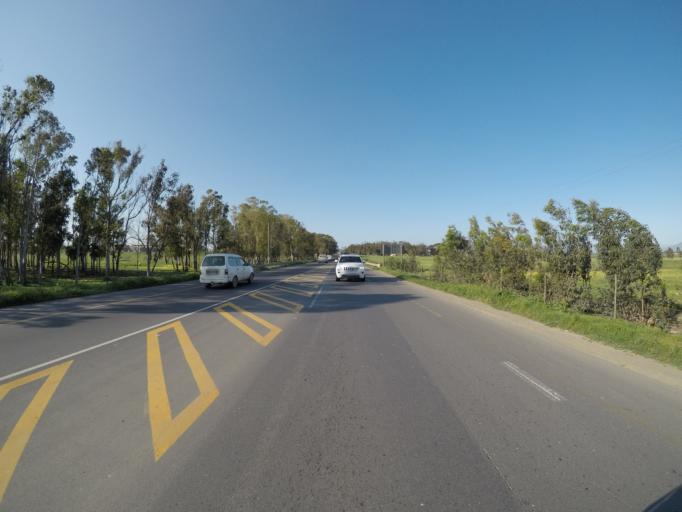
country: ZA
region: Western Cape
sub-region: City of Cape Town
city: Kraaifontein
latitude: -33.7984
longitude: 18.6892
